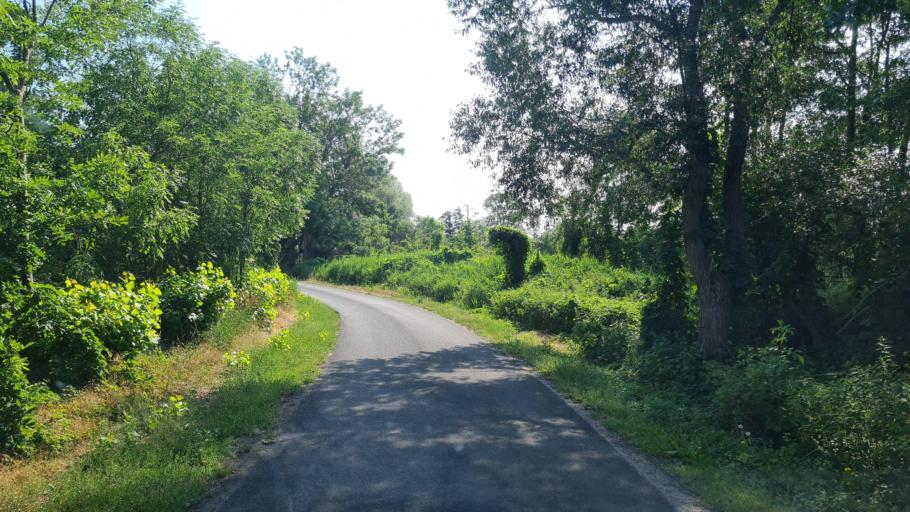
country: DE
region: Brandenburg
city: Wollin
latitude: 52.3245
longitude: 12.5375
